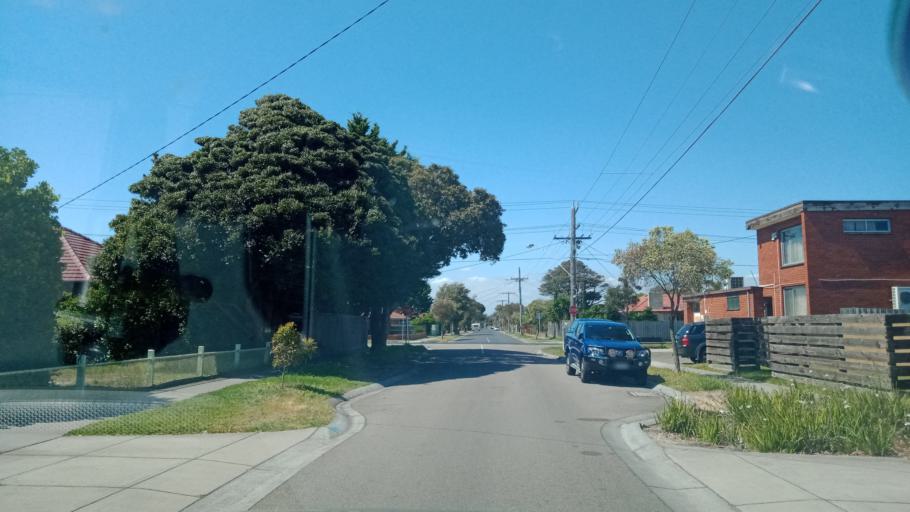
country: AU
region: Victoria
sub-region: Kingston
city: Chelsea
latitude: -38.0529
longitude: 145.1212
